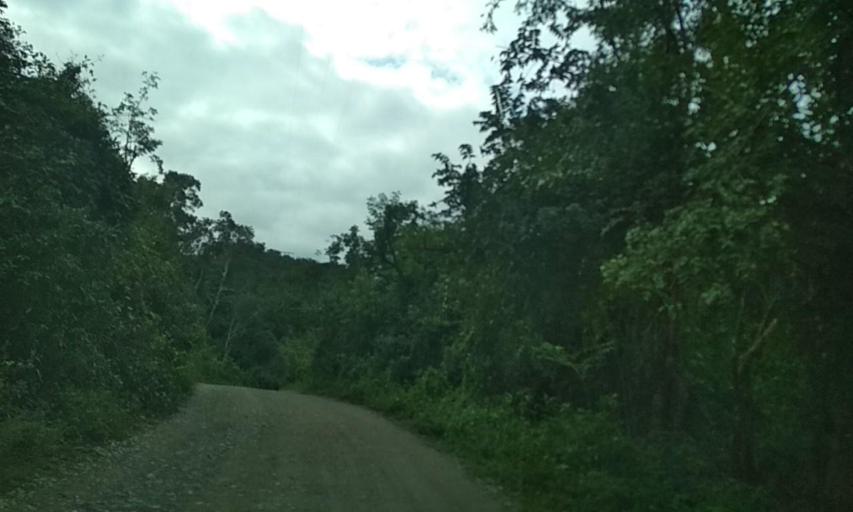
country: MX
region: Veracruz
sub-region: Papantla
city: Residencial Tajin
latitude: 20.6187
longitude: -97.3611
